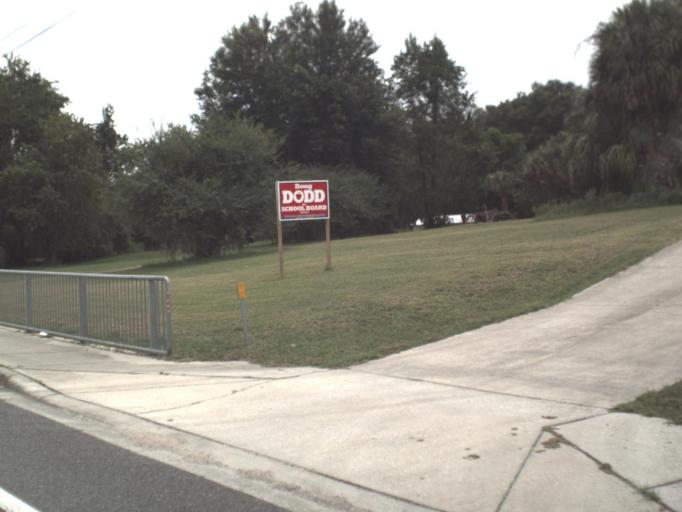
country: US
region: Florida
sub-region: Citrus County
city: Inverness
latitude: 28.8404
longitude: -82.2987
